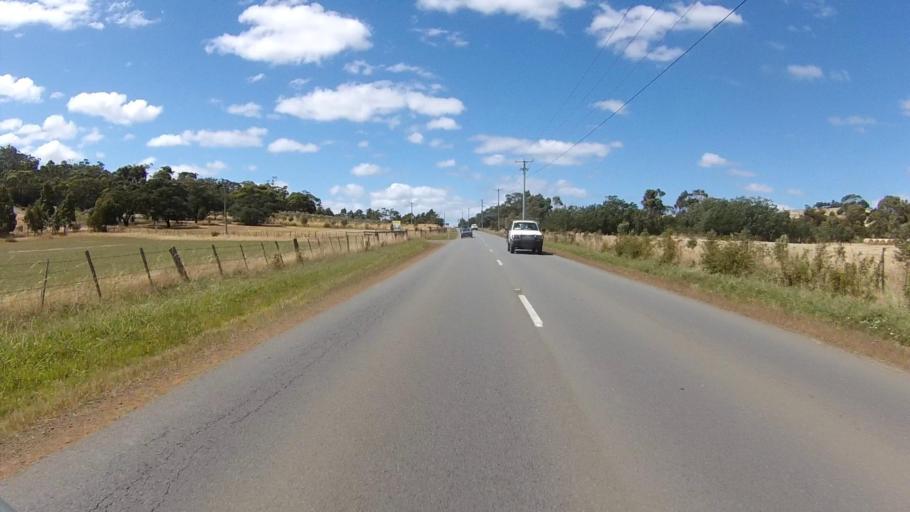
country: AU
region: Tasmania
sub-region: Clarence
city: Cambridge
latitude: -42.8192
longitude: 147.4394
